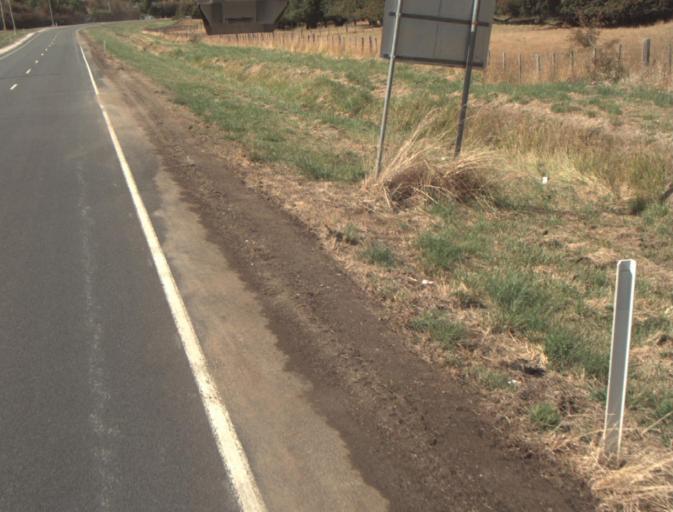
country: AU
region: Tasmania
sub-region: Launceston
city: Mayfield
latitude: -41.2569
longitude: 147.2170
